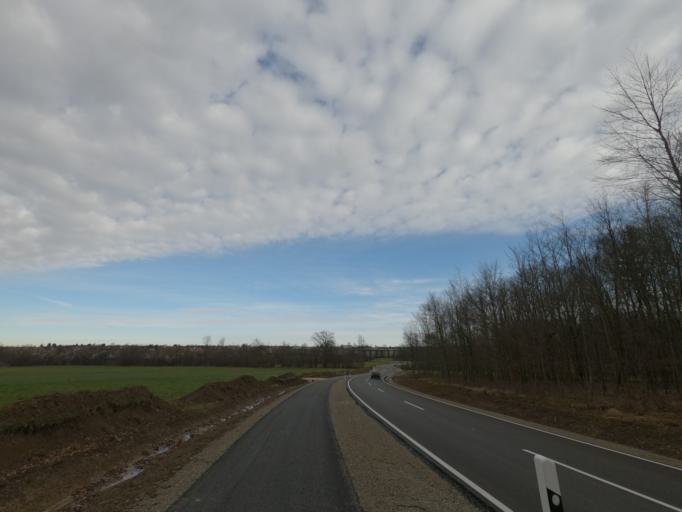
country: DE
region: Baden-Wuerttemberg
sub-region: Regierungsbezirk Stuttgart
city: Schlierbach
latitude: 48.6666
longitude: 9.5289
